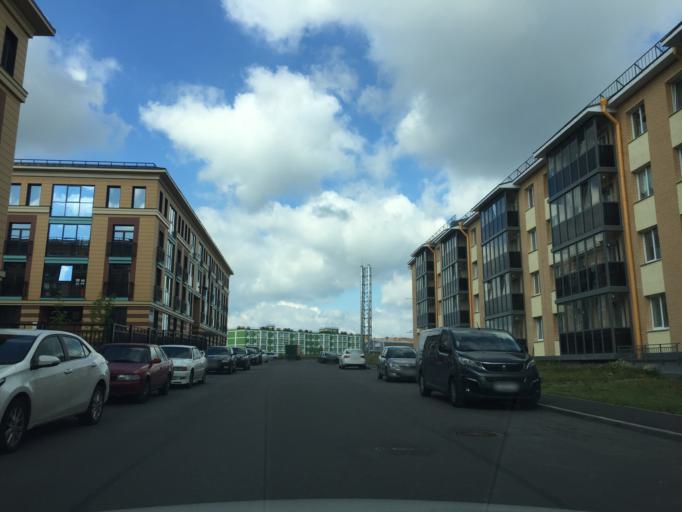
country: RU
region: St.-Petersburg
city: Pushkin
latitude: 59.7539
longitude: 30.3751
